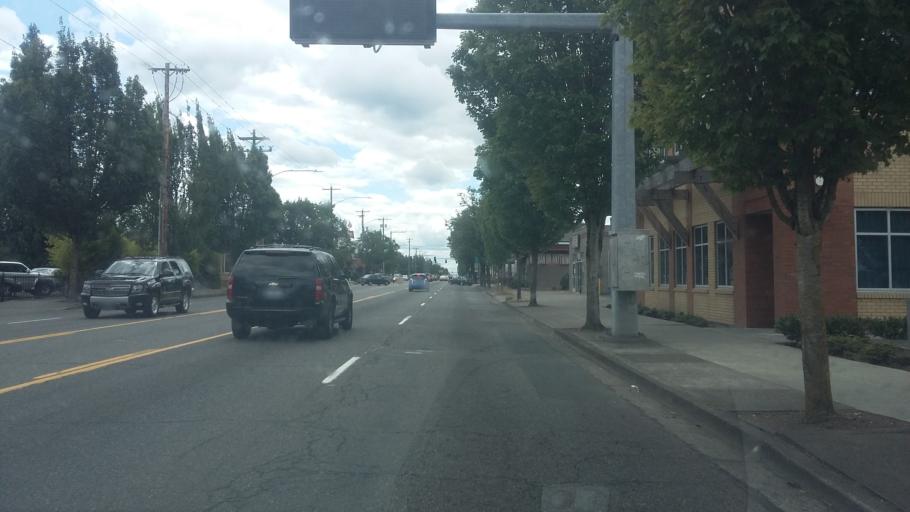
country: US
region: Oregon
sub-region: Multnomah County
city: Lents
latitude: 45.4998
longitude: -122.5788
